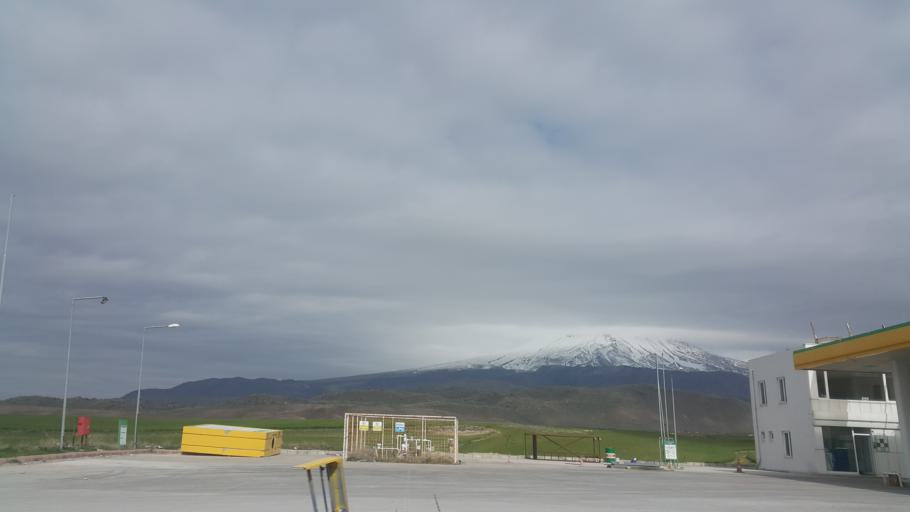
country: TR
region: Aksaray
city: Taspinar
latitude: 38.1512
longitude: 34.0350
